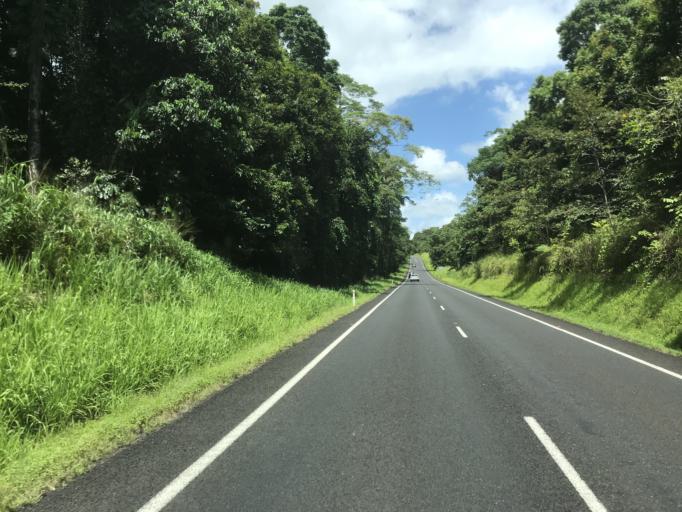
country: AU
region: Queensland
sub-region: Cassowary Coast
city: Innisfail
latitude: -17.6113
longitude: 145.7909
